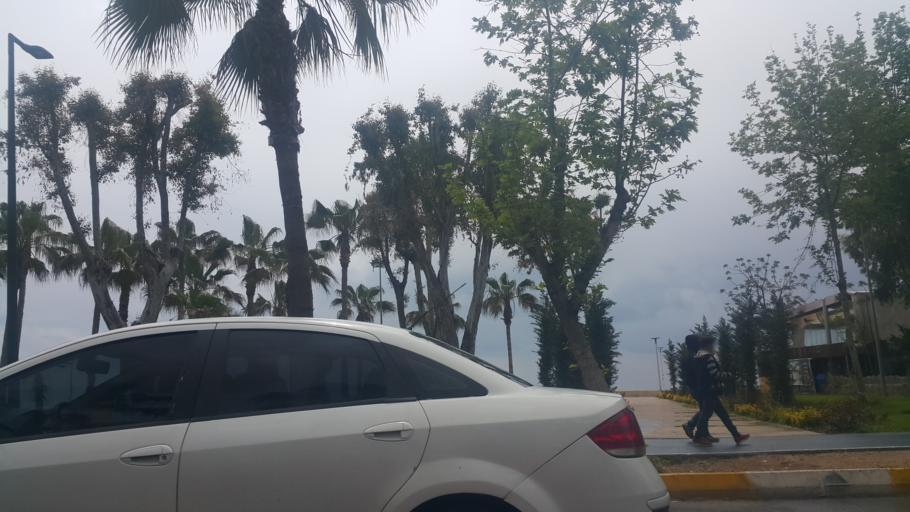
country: TR
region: Mersin
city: Mercin
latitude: 36.7794
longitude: 34.5924
